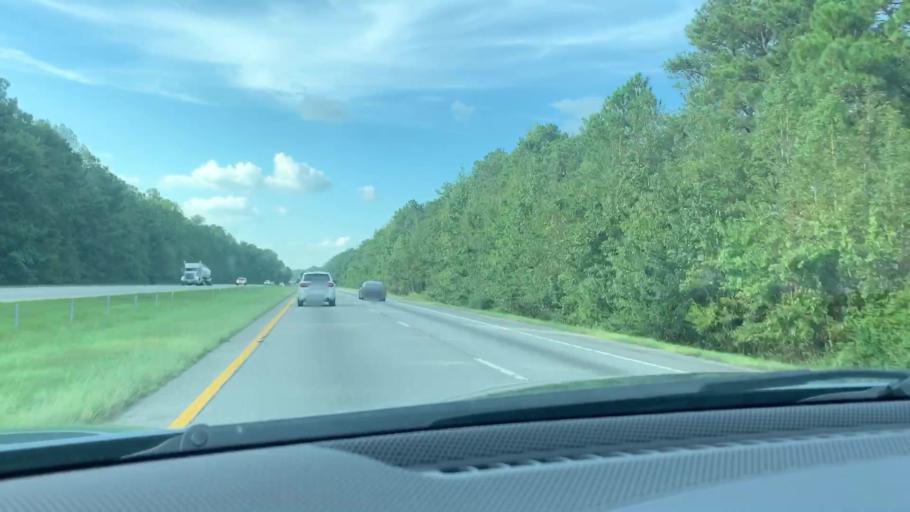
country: US
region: South Carolina
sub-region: Orangeburg County
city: Brookdale
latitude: 33.4872
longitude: -80.7605
